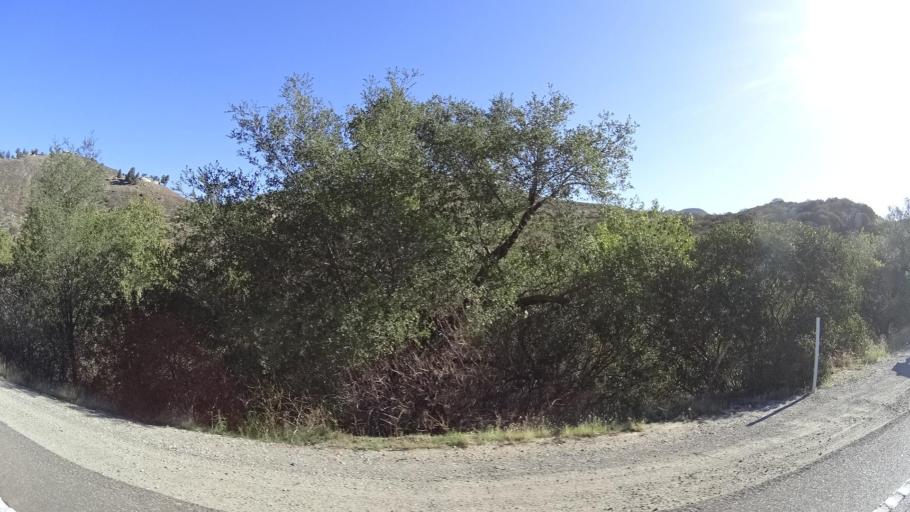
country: US
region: California
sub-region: San Diego County
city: Jamul
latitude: 32.6538
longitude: -116.7923
